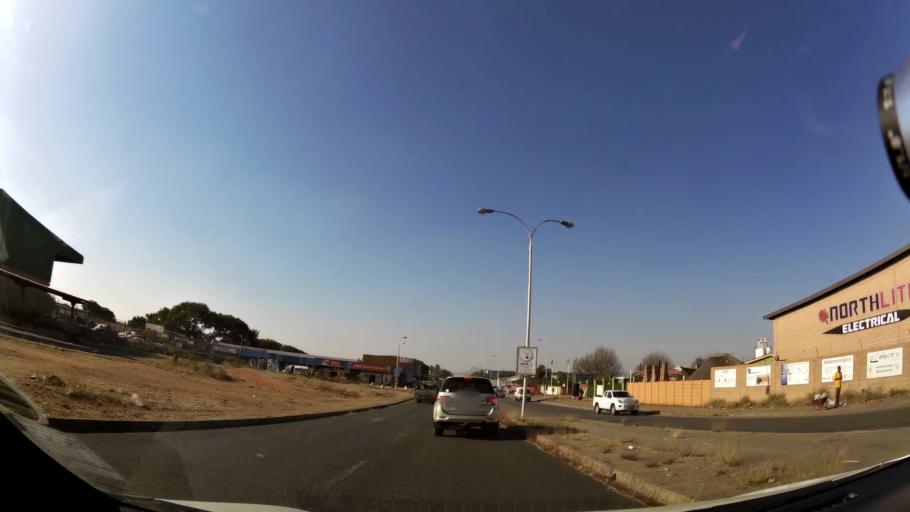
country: ZA
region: North-West
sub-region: Bojanala Platinum District Municipality
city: Rustenburg
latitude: -25.6687
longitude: 27.2573
